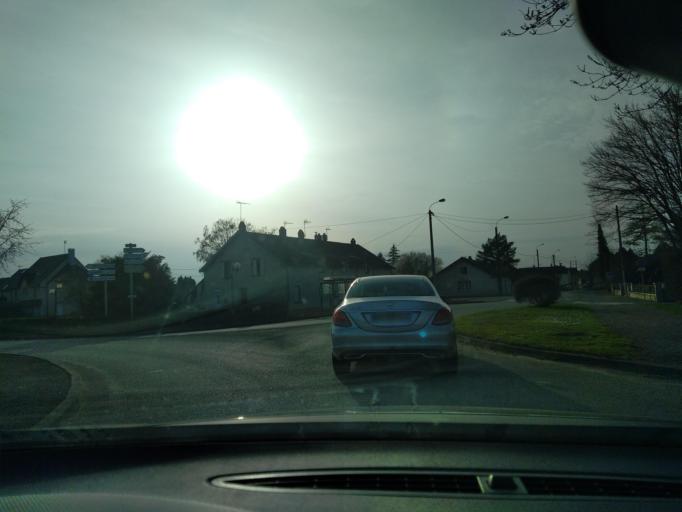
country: FR
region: Franche-Comte
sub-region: Departement du Jura
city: Chaussin
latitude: 46.9668
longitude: 5.4154
